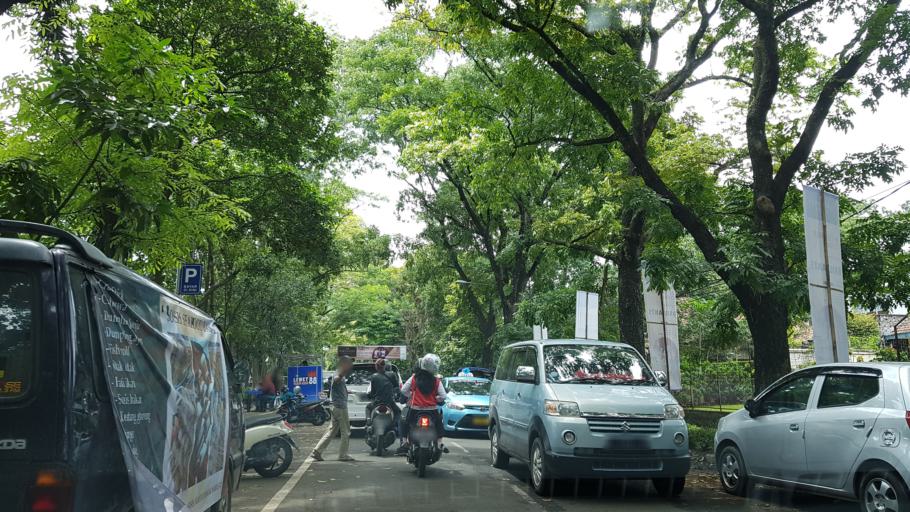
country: ID
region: West Java
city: Bandung
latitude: -6.8918
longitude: 107.6161
